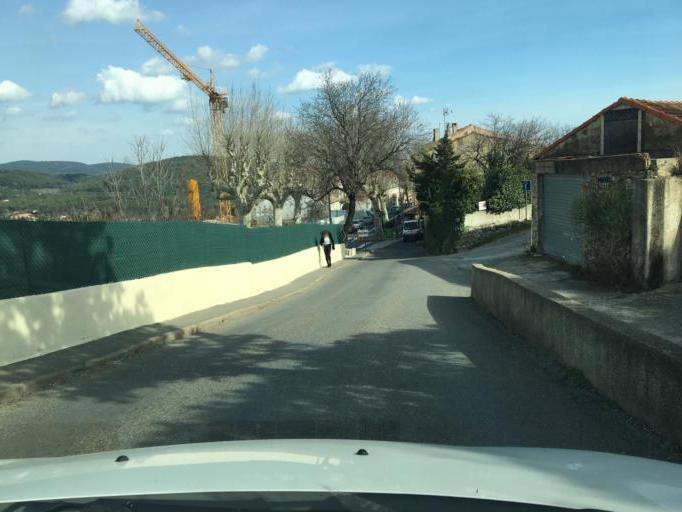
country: FR
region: Provence-Alpes-Cote d'Azur
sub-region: Departement du Var
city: Flayosc
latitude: 43.5347
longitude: 6.3928
